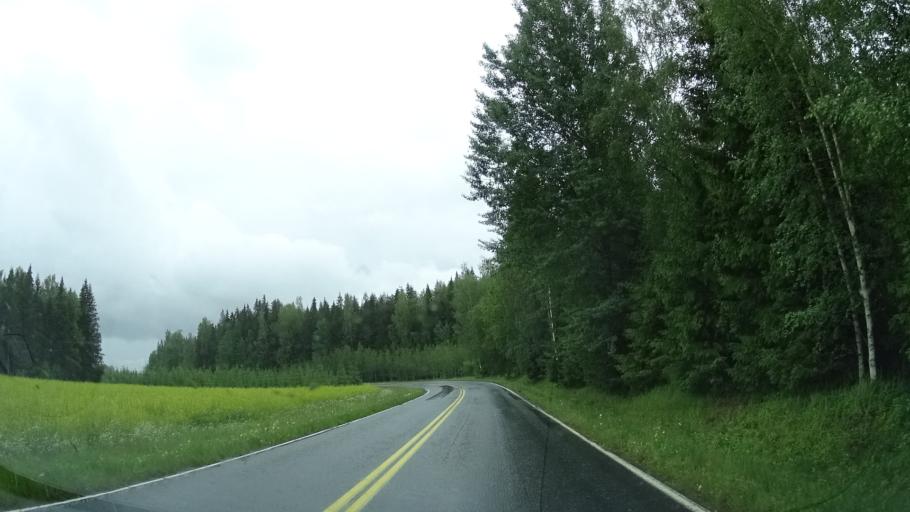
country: FI
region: Haeme
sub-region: Forssa
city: Humppila
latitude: 60.9911
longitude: 23.2565
